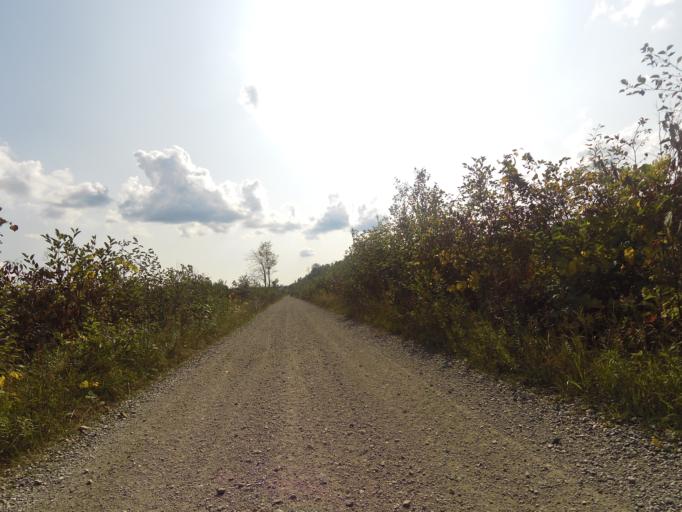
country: CA
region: Ontario
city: Renfrew
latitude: 45.1312
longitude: -76.6874
